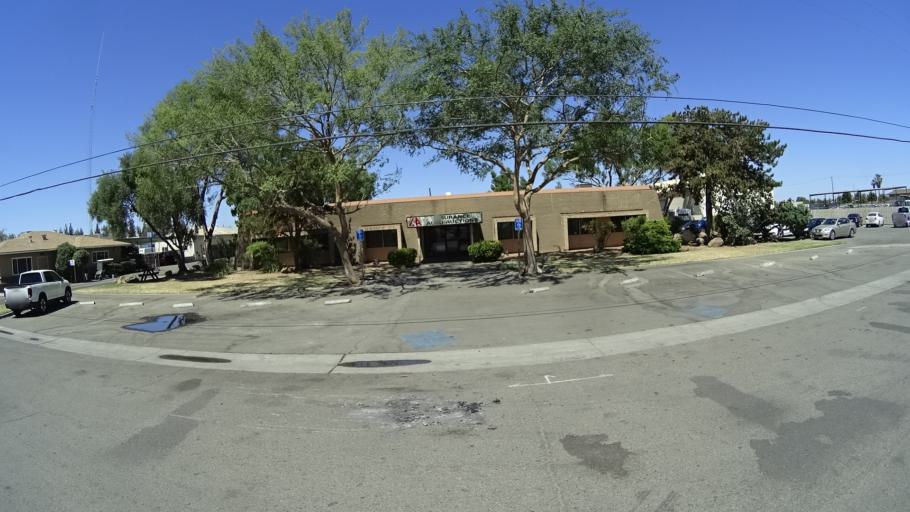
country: US
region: California
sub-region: Fresno County
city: West Park
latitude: 36.7671
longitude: -119.8378
